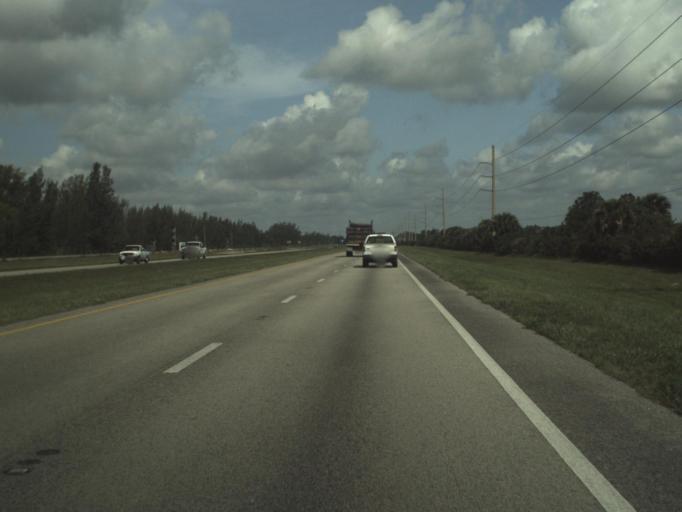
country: US
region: Florida
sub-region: Palm Beach County
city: Palm Beach Gardens
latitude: 26.8435
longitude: -80.2023
